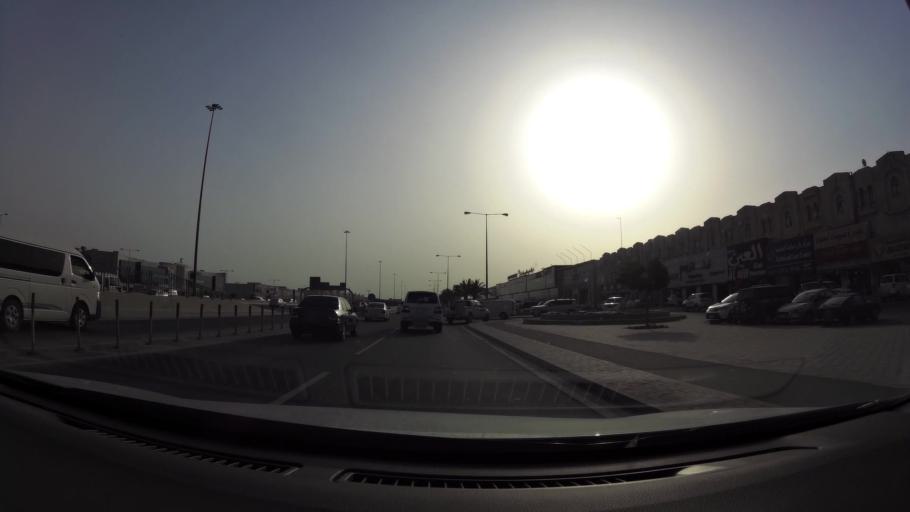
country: QA
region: Baladiyat ar Rayyan
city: Ar Rayyan
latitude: 25.2424
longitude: 51.4598
